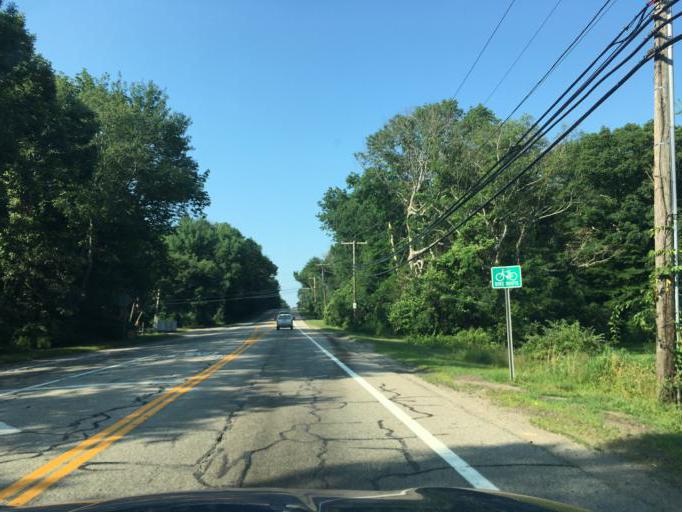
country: US
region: Rhode Island
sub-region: Washington County
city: Exeter
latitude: 41.5332
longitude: -71.5470
